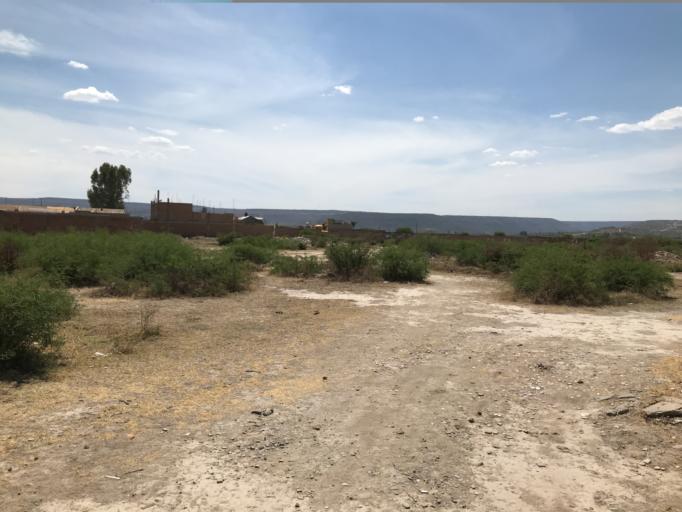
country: MX
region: Durango
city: Victoria de Durango
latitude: 23.9808
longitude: -104.6860
